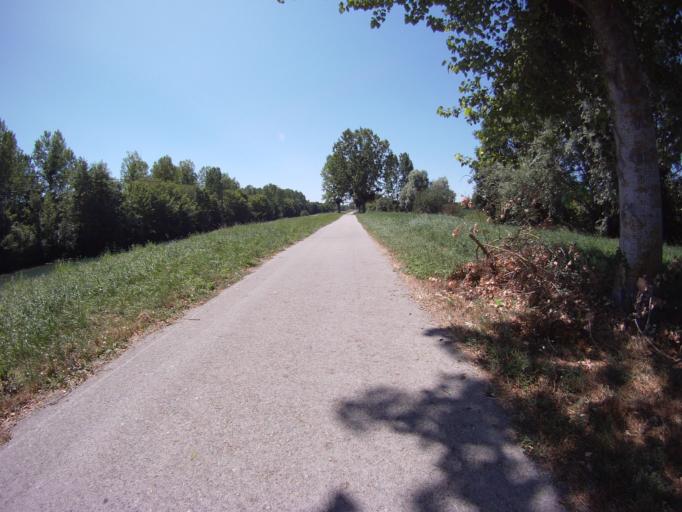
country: FR
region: Champagne-Ardenne
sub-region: Departement de la Marne
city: Damery
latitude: 49.0742
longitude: 3.8535
